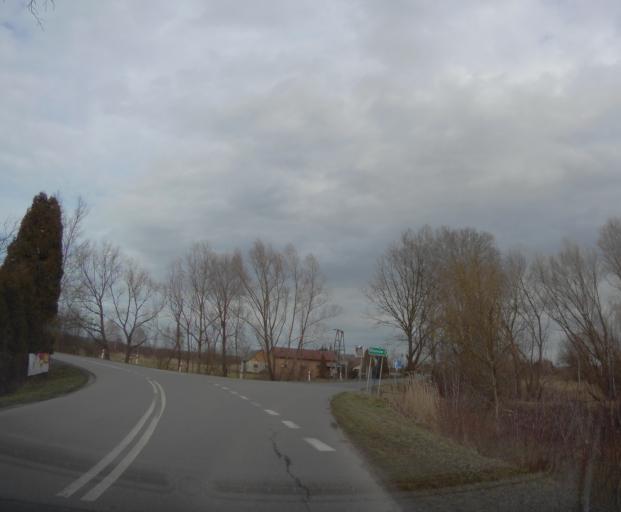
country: PL
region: Subcarpathian Voivodeship
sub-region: Powiat nizanski
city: Ulanow
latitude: 50.4740
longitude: 22.2494
